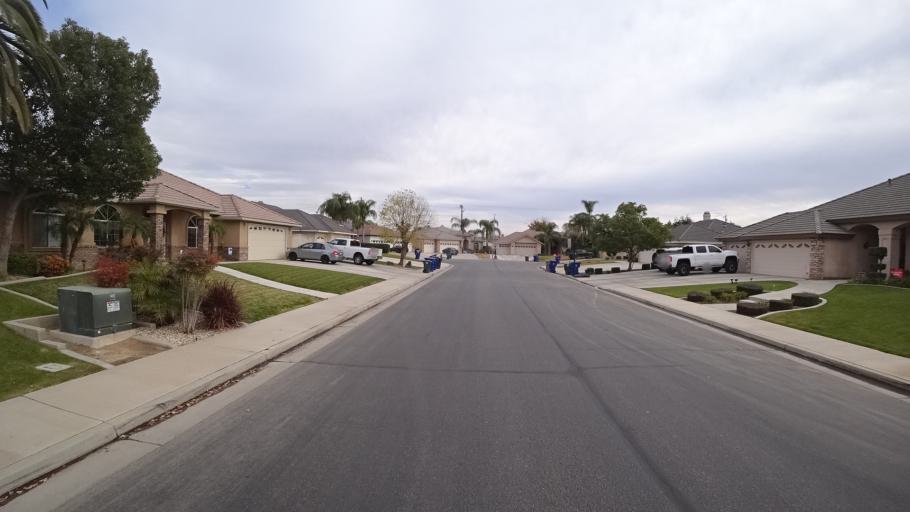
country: US
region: California
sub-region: Kern County
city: Rosedale
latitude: 35.4192
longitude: -119.1291
